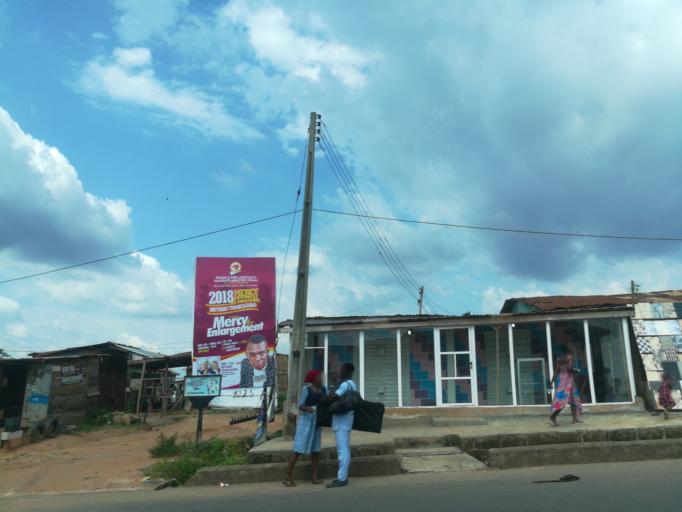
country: NG
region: Oyo
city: Ibadan
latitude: 7.4276
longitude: 3.8400
